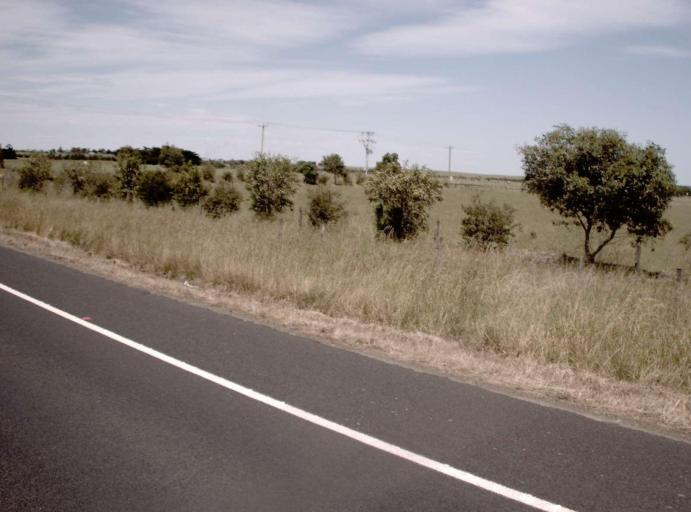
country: AU
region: Victoria
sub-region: Wellington
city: Heyfield
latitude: -38.1096
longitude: 146.8909
